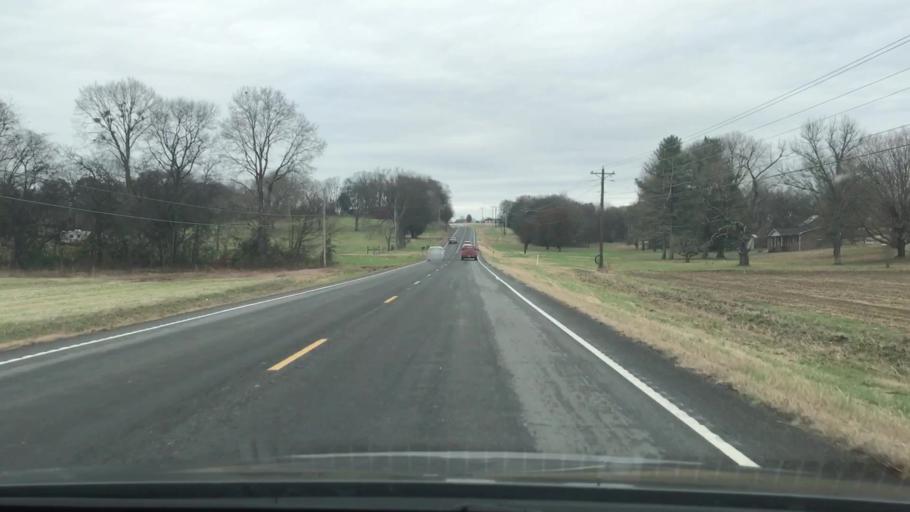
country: US
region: Tennessee
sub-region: Trousdale County
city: Hartsville
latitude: 36.3898
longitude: -86.2494
